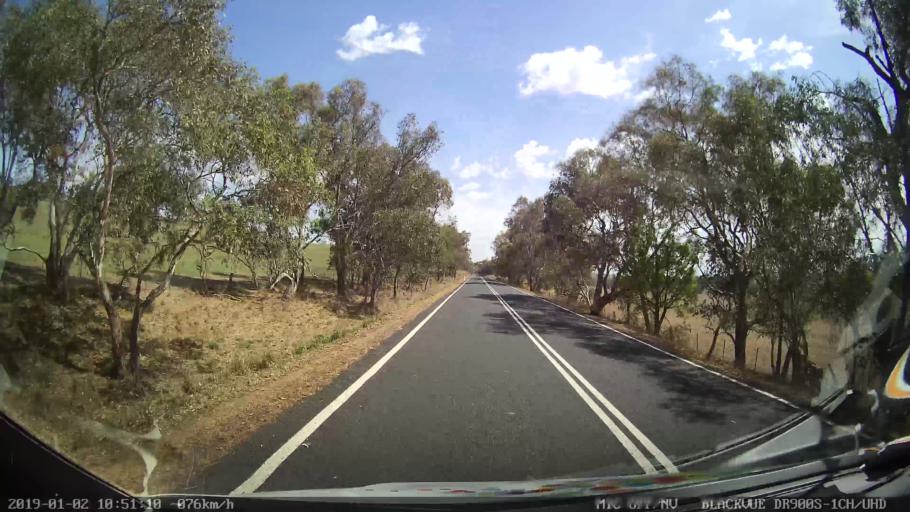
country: AU
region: New South Wales
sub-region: Cootamundra
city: Cootamundra
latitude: -34.7031
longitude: 148.2762
